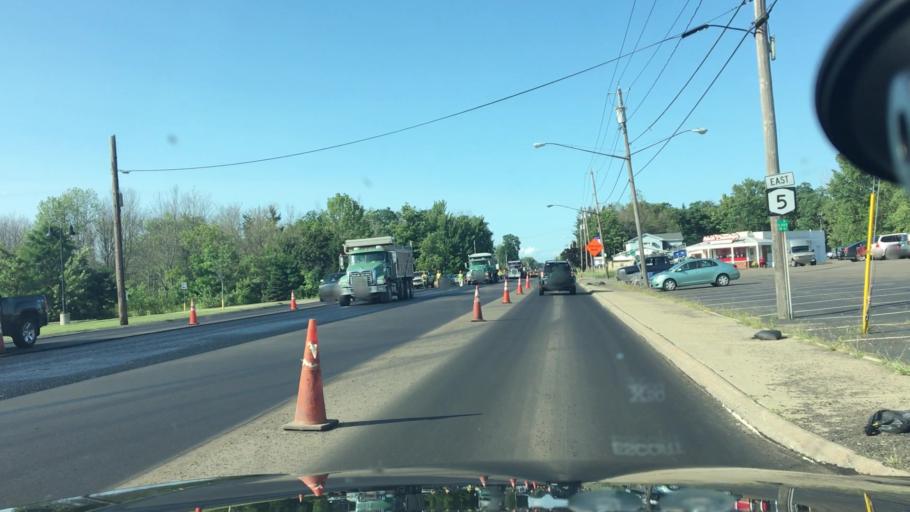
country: US
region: New York
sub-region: Erie County
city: Angola on the Lake
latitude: 42.6387
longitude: -79.0478
